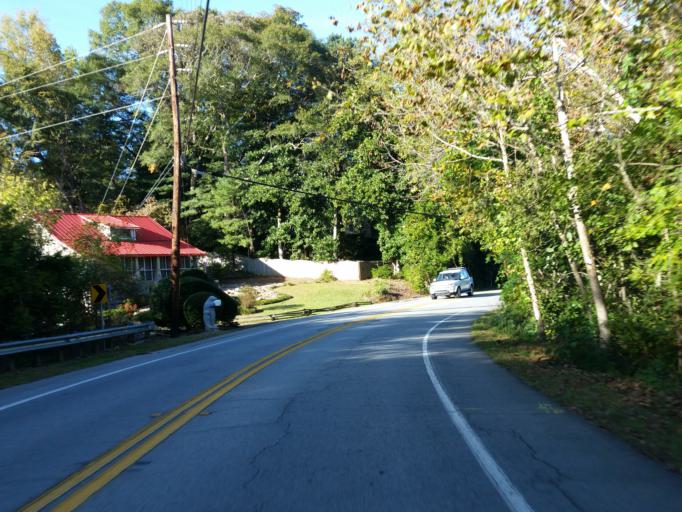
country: US
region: Georgia
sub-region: Fulton County
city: Roswell
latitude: 34.0002
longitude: -84.3850
